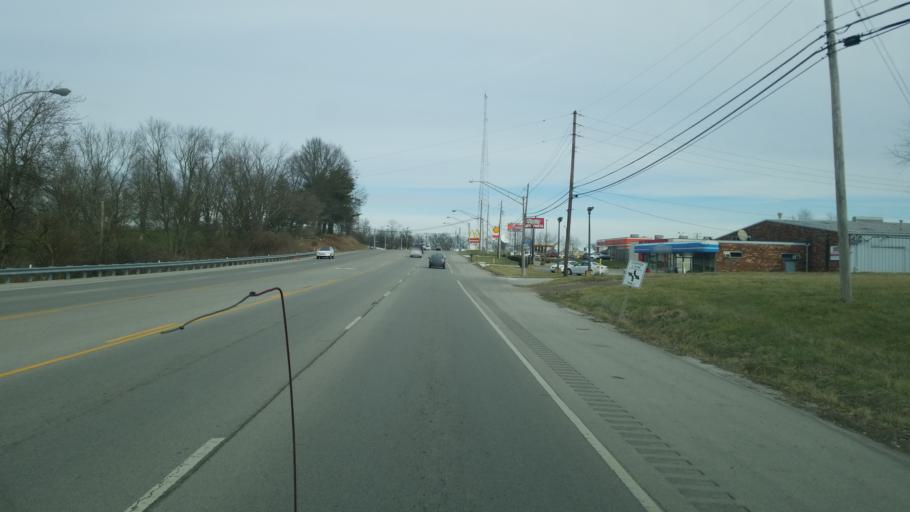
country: US
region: Ohio
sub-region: Brown County
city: Aberdeen
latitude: 38.6413
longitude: -83.7824
